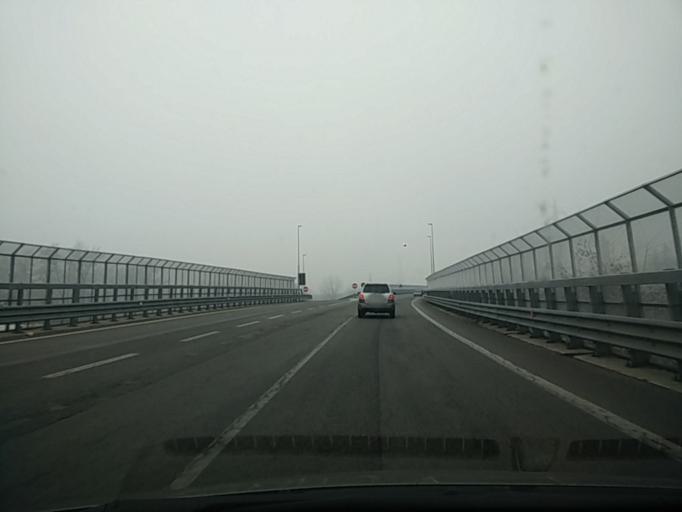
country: IT
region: Veneto
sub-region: Provincia di Belluno
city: Seren del Grappa
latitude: 46.0008
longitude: 11.8430
